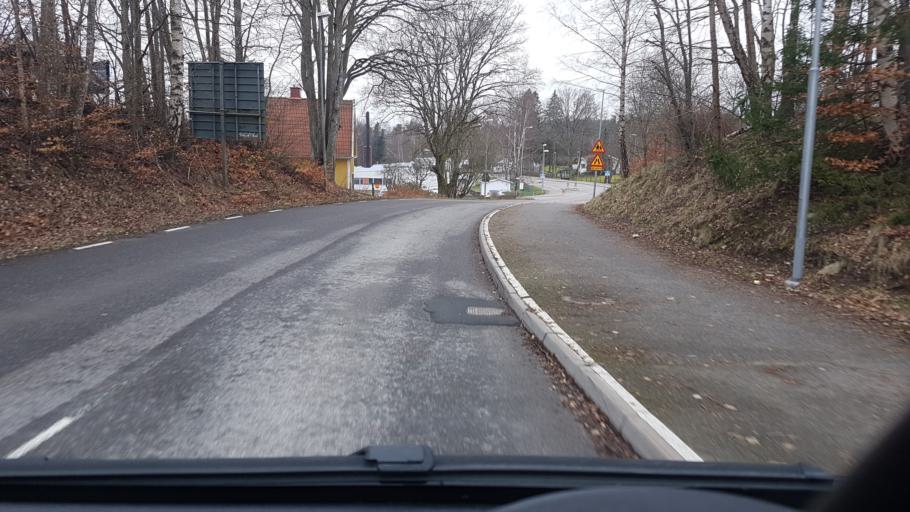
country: SE
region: Vaestra Goetaland
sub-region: Lerums Kommun
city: Stenkullen
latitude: 57.7991
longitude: 12.3697
